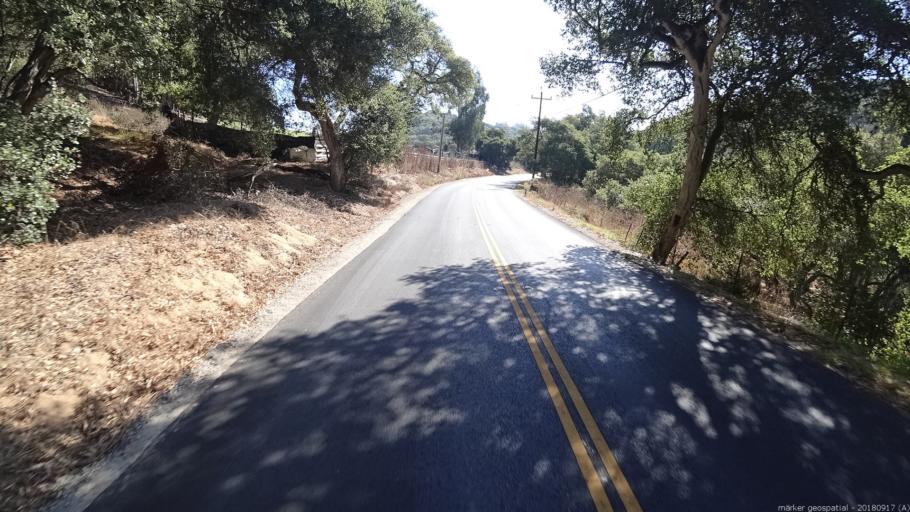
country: US
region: California
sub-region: Monterey County
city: Elkhorn
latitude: 36.8155
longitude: -121.7220
